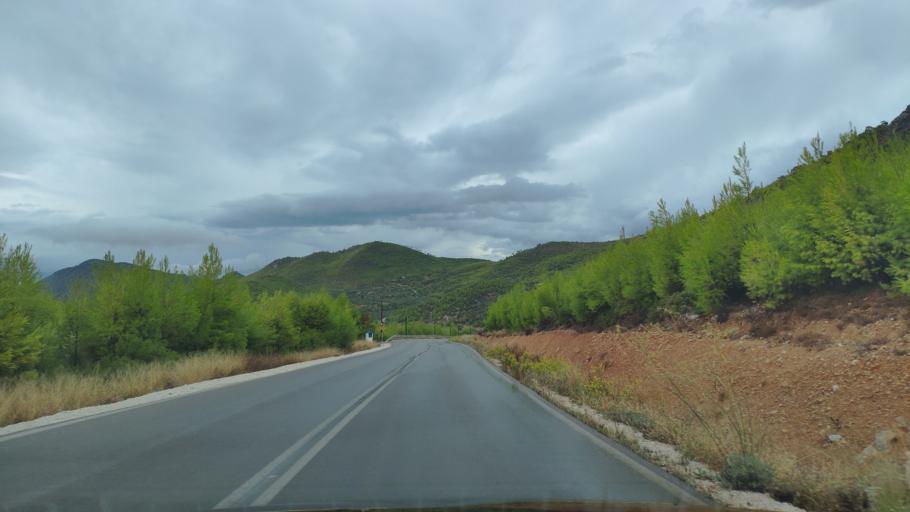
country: GR
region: Peloponnese
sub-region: Nomos Korinthias
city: Perachora
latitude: 38.0298
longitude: 22.9301
